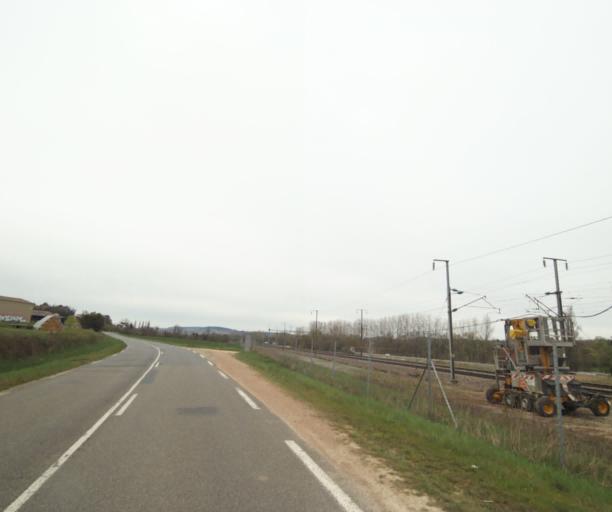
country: FR
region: Bourgogne
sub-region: Departement de Saone-et-Loire
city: Charnay-les-Macon
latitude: 46.2901
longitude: 4.7736
